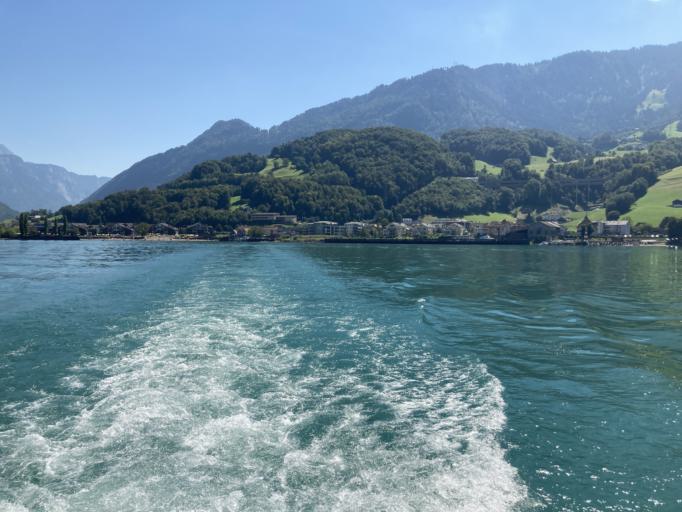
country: CH
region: Saint Gallen
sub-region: Wahlkreis Sarganserland
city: Quarten
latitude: 47.1169
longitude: 9.2480
